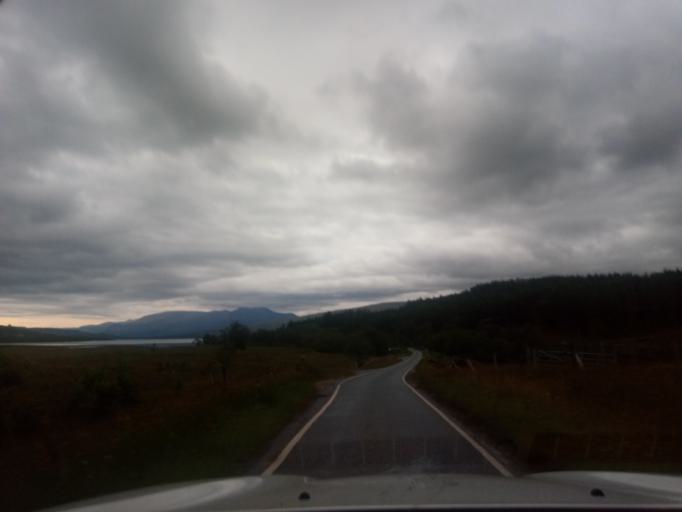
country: GB
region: Scotland
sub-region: Highland
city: Fort William
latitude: 56.8567
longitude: -5.3484
